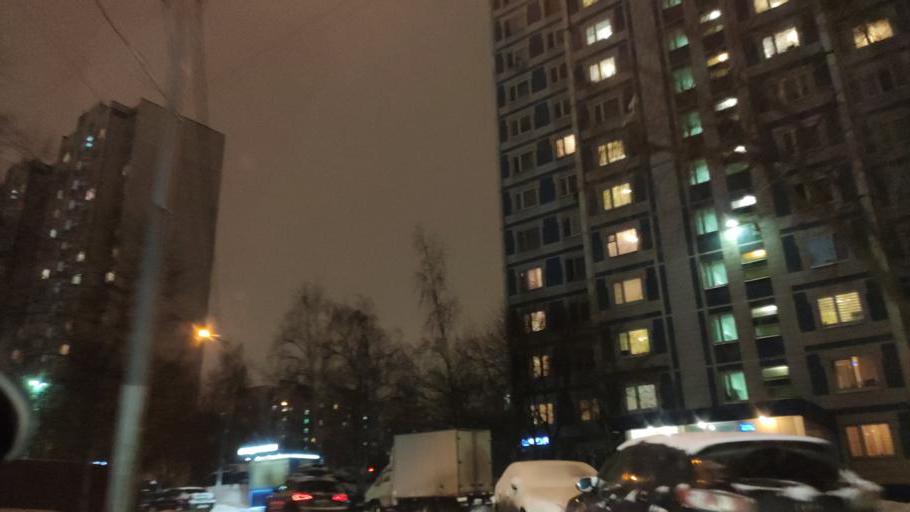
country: RU
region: Moscow
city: Tyoply Stan
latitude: 55.6244
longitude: 37.4902
